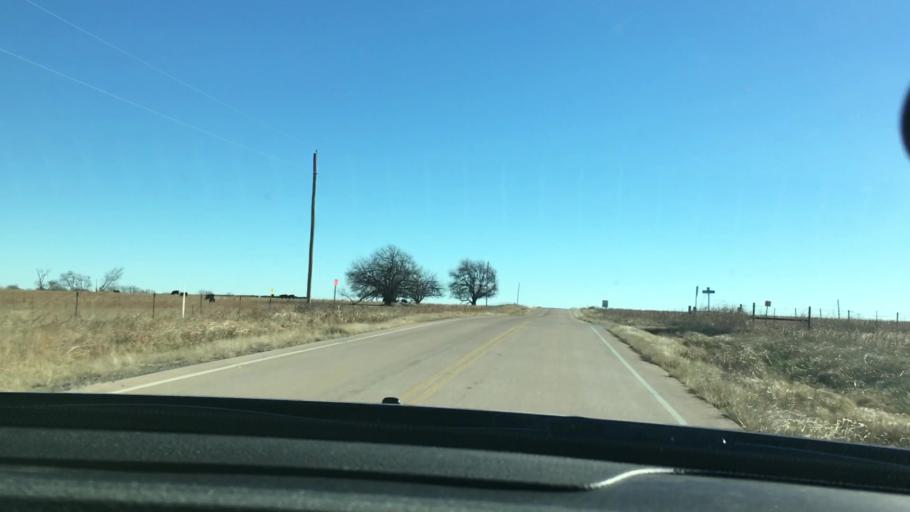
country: US
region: Oklahoma
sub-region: Marshall County
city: Madill
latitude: 34.1144
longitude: -96.7242
